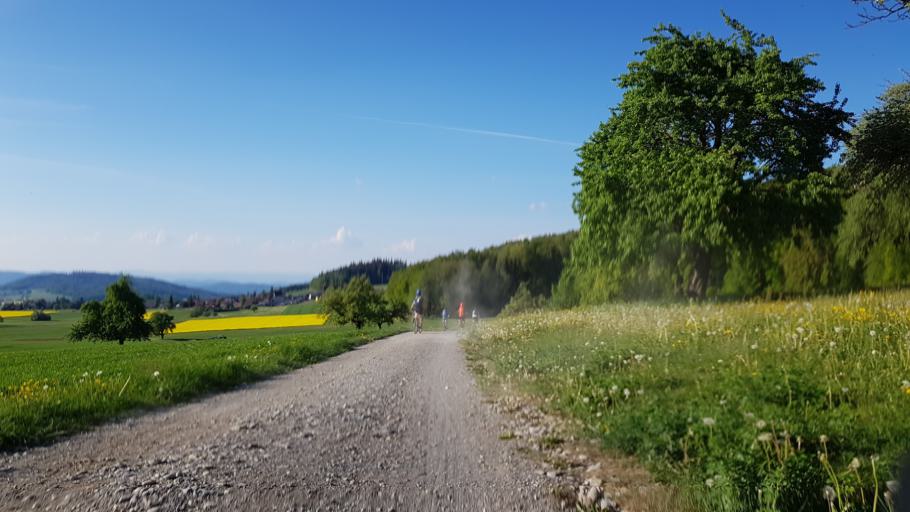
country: CH
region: Aargau
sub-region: Bezirk Muri
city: Buttwil
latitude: 47.2768
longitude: 8.2757
